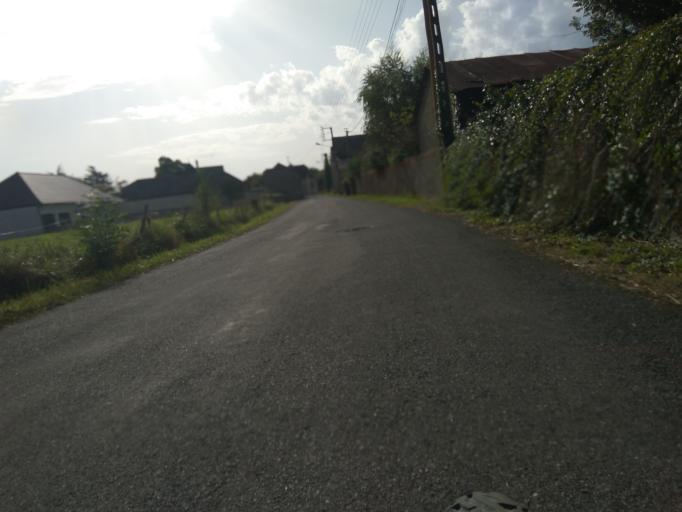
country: FR
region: Aquitaine
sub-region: Departement des Pyrenees-Atlantiques
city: Mazeres-Lezons
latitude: 43.2732
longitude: -0.3496
